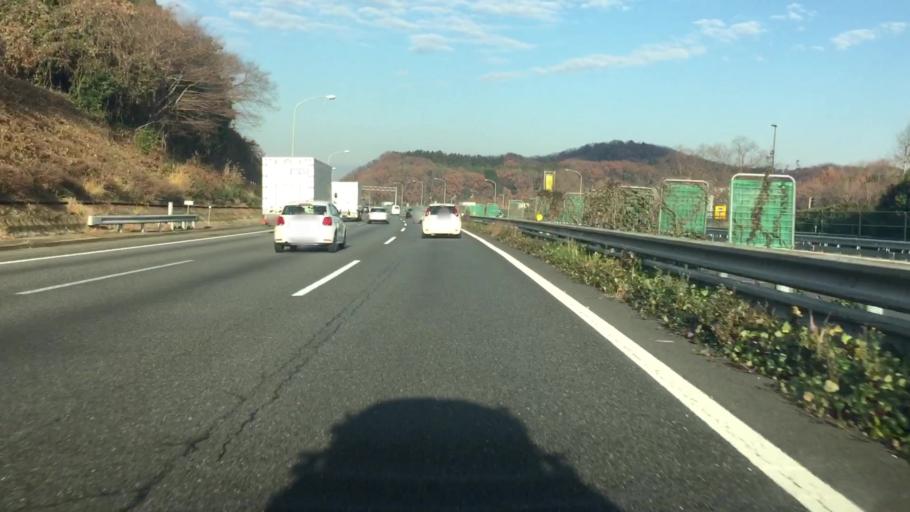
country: JP
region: Saitama
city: Ogawa
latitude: 36.0826
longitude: 139.2969
